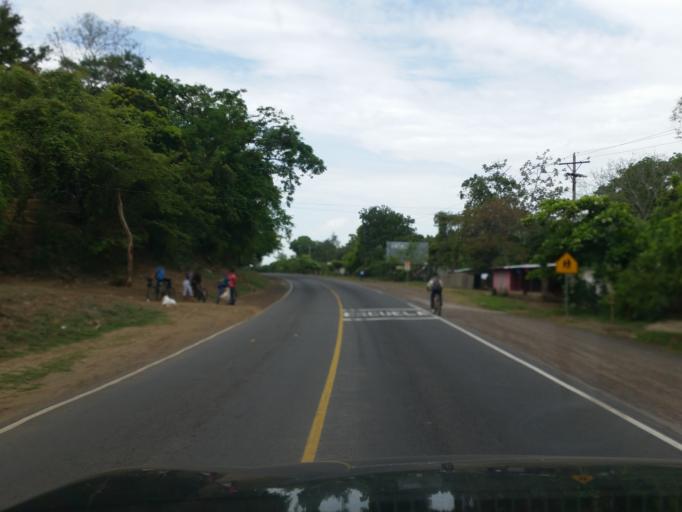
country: NI
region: Granada
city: Diriomo
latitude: 11.8437
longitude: -86.0287
